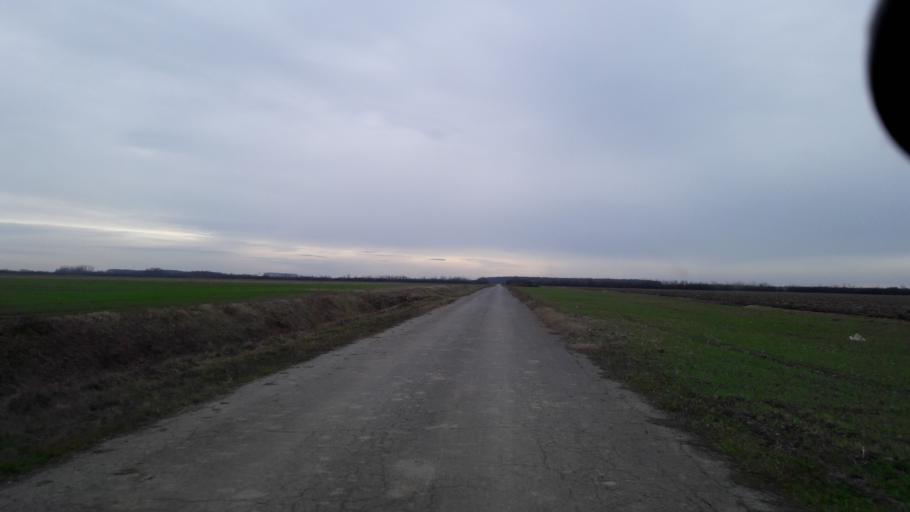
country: HR
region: Osjecko-Baranjska
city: Vladislavci
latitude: 45.4371
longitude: 18.5696
